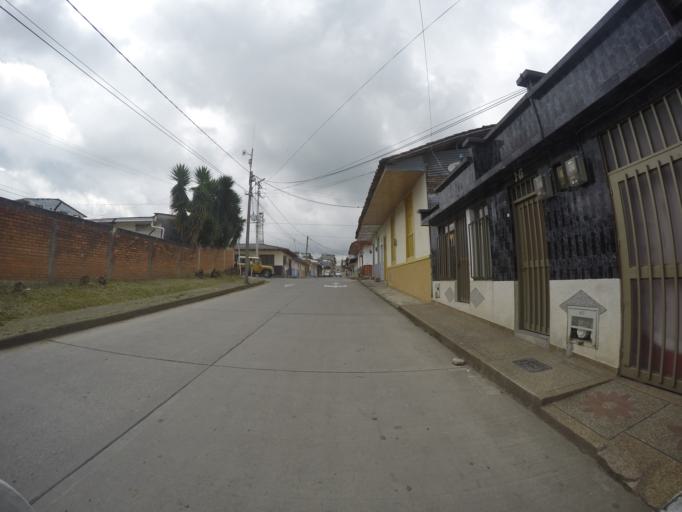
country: CO
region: Quindio
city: Filandia
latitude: 4.6726
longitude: -75.6594
